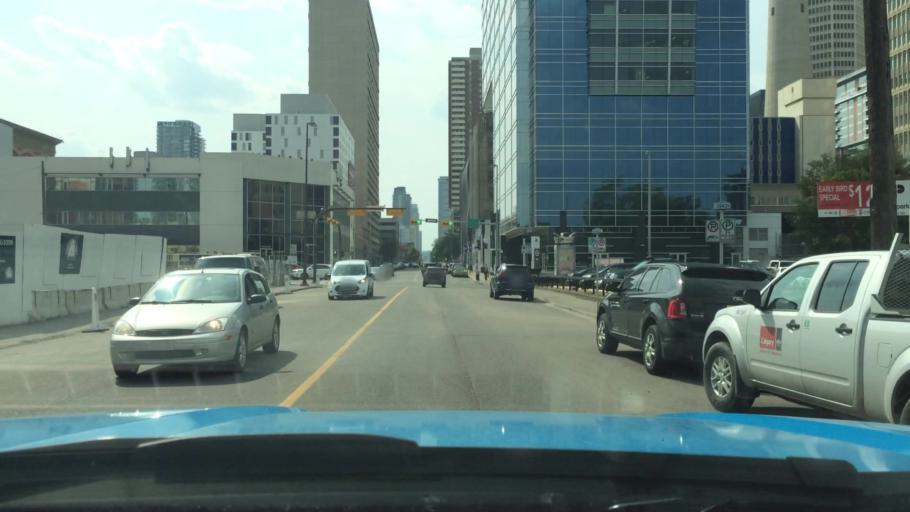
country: CA
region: Alberta
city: Calgary
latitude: 51.0433
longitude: -114.0596
